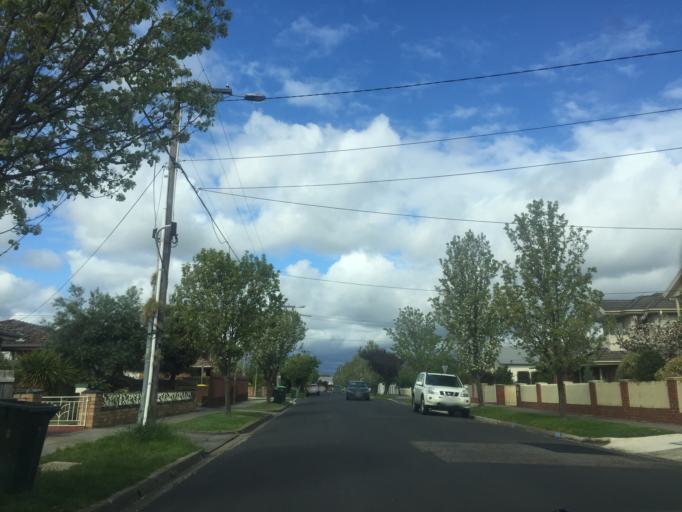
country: AU
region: Victoria
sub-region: Darebin
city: Reservoir
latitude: -37.7253
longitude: 145.0085
